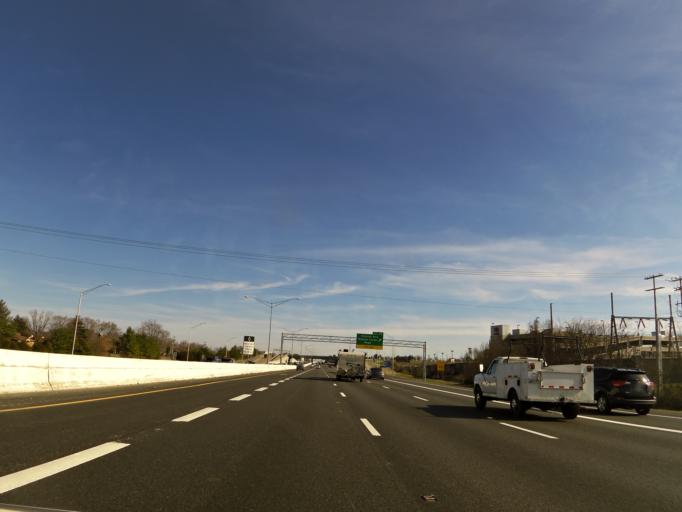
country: US
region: Tennessee
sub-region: Rutherford County
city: Murfreesboro
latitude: 35.8713
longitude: -86.4618
